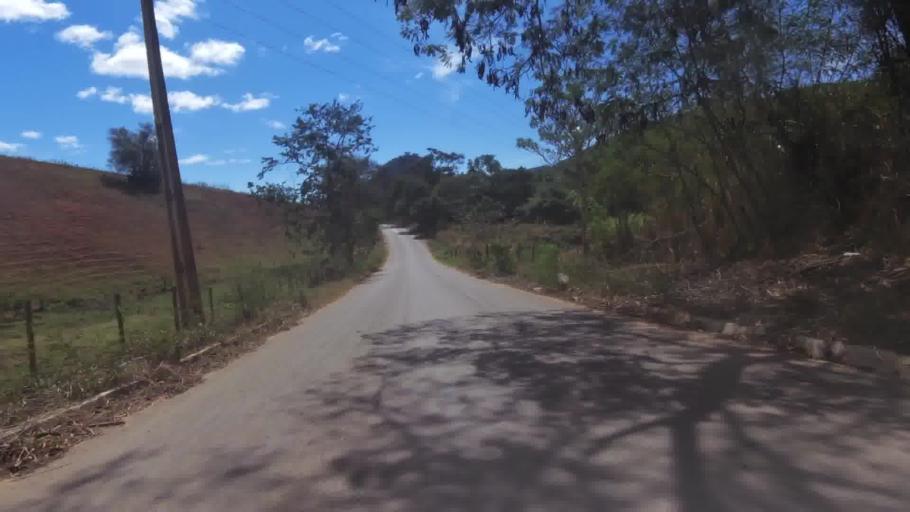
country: BR
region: Espirito Santo
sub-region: Cachoeiro De Itapemirim
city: Cachoeiro de Itapemirim
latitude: -20.9315
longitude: -41.2141
